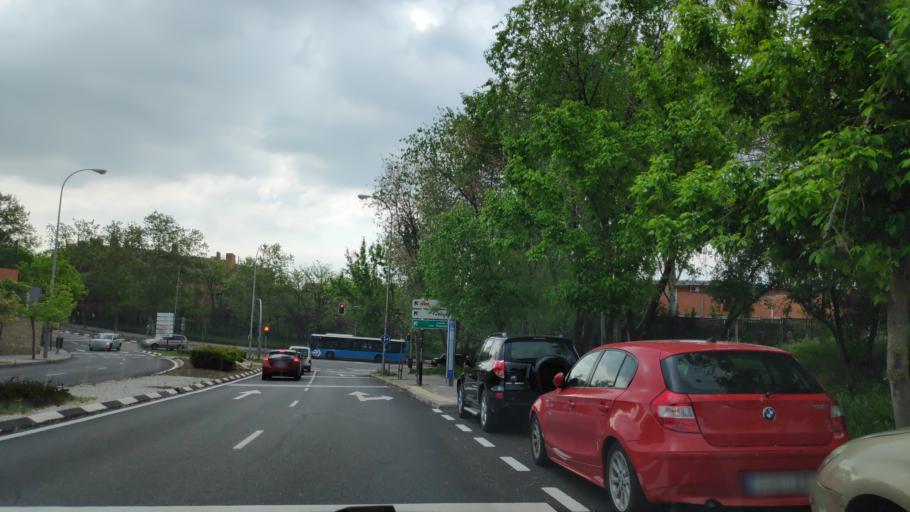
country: ES
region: Madrid
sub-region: Provincia de Madrid
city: Pozuelo de Alarcon
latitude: 40.4561
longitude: -3.7859
